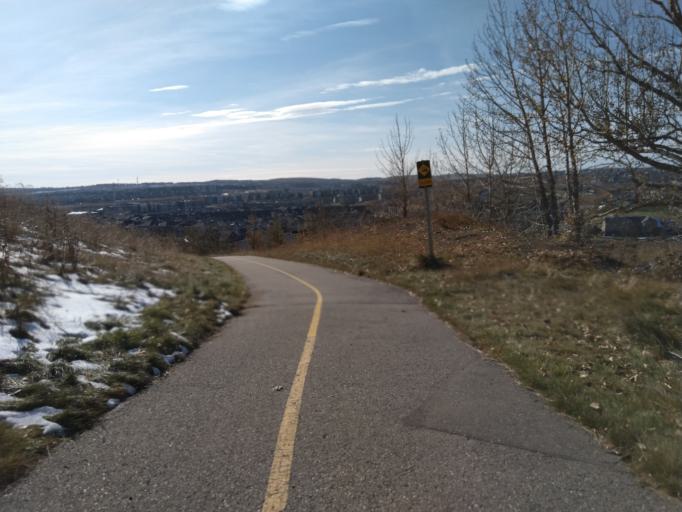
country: CA
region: Alberta
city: Calgary
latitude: 51.1760
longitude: -114.1246
